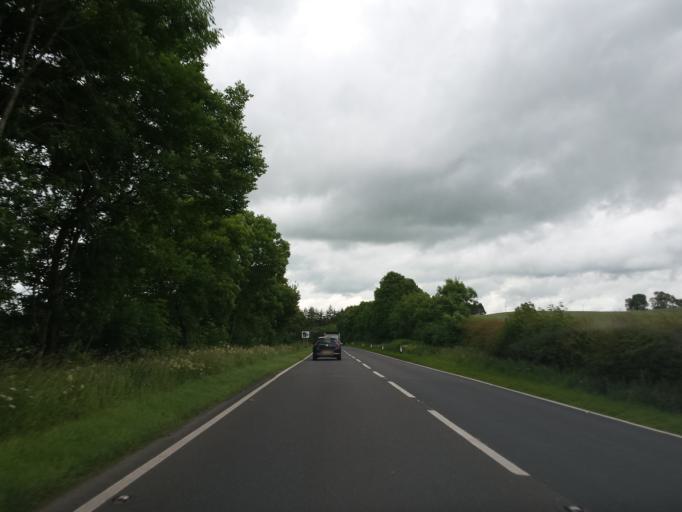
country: GB
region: Scotland
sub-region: Dumfries and Galloway
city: Dalbeattie
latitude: 55.0284
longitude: -3.8381
